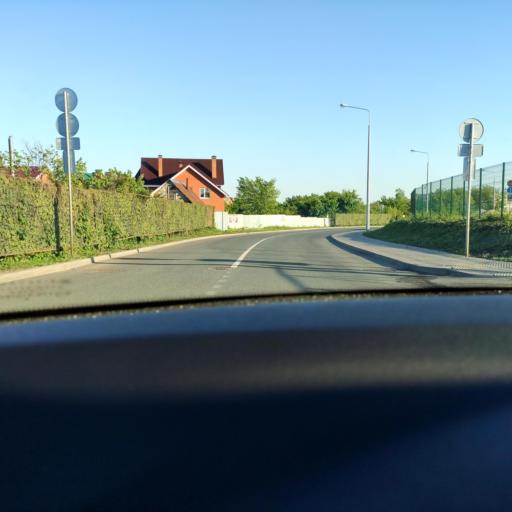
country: RU
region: Samara
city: Petra-Dubrava
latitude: 53.2752
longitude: 50.2593
